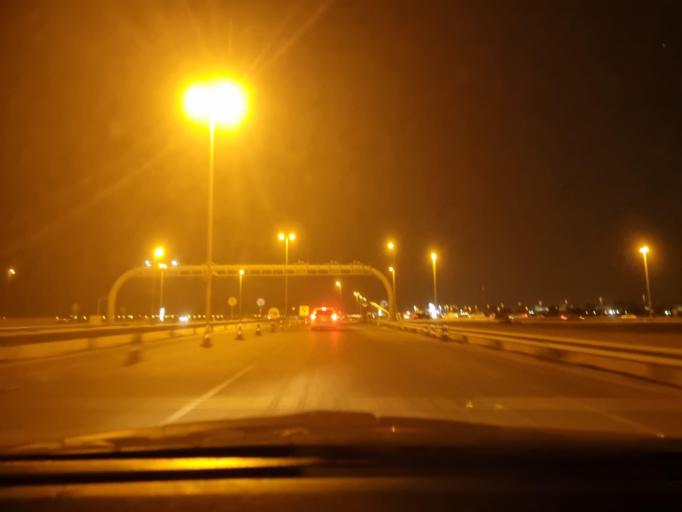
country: AE
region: Abu Dhabi
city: Abu Dhabi
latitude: 24.3614
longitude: 54.6678
